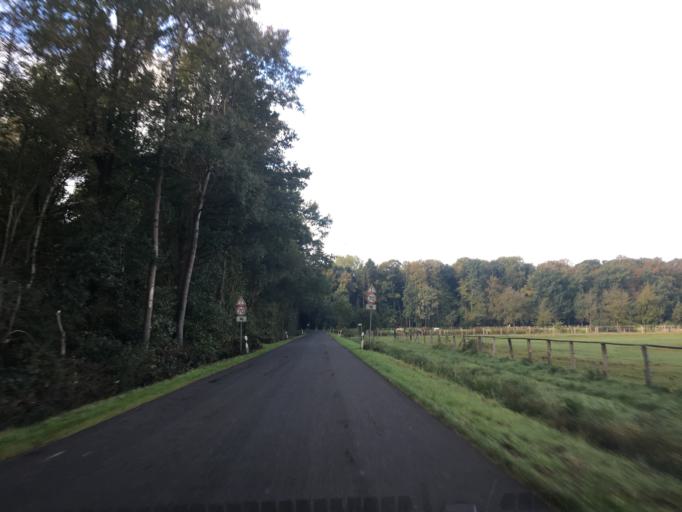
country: DE
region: North Rhine-Westphalia
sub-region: Regierungsbezirk Munster
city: Havixbeck
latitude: 51.9778
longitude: 7.4563
